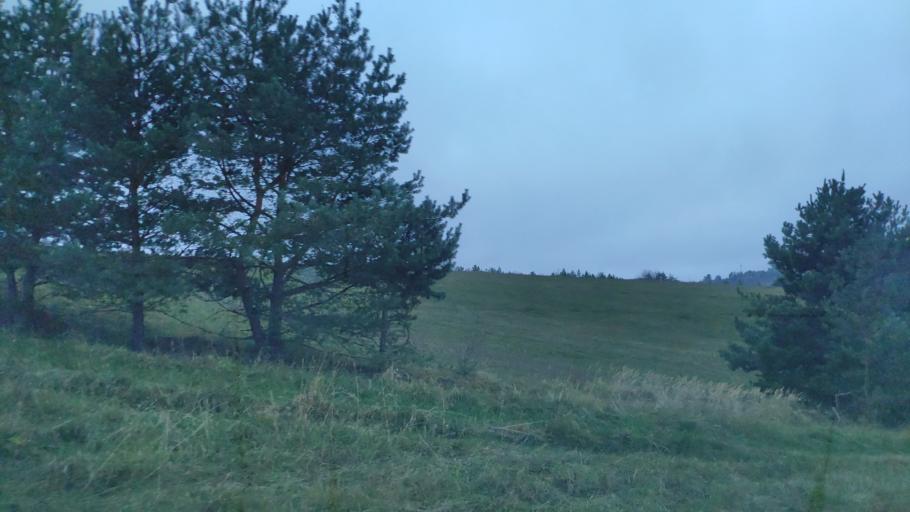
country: SK
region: Presovsky
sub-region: Okres Presov
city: Presov
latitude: 48.9392
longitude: 21.0862
